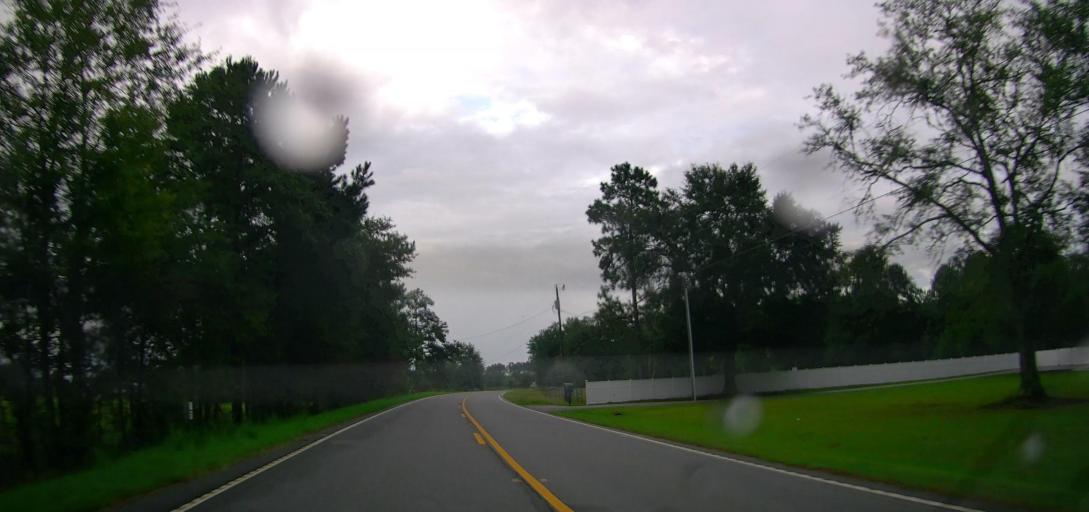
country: US
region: Georgia
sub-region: Ware County
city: Deenwood
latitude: 31.2851
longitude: -82.4340
